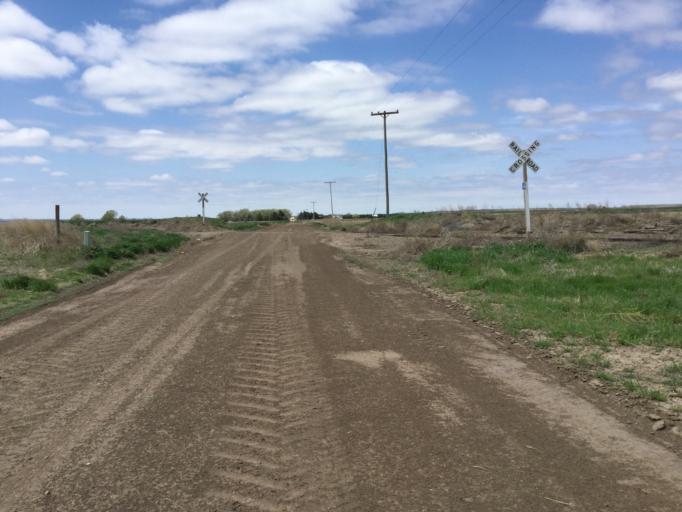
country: US
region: Kansas
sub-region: Osborne County
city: Osborne
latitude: 39.4516
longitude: -98.6028
